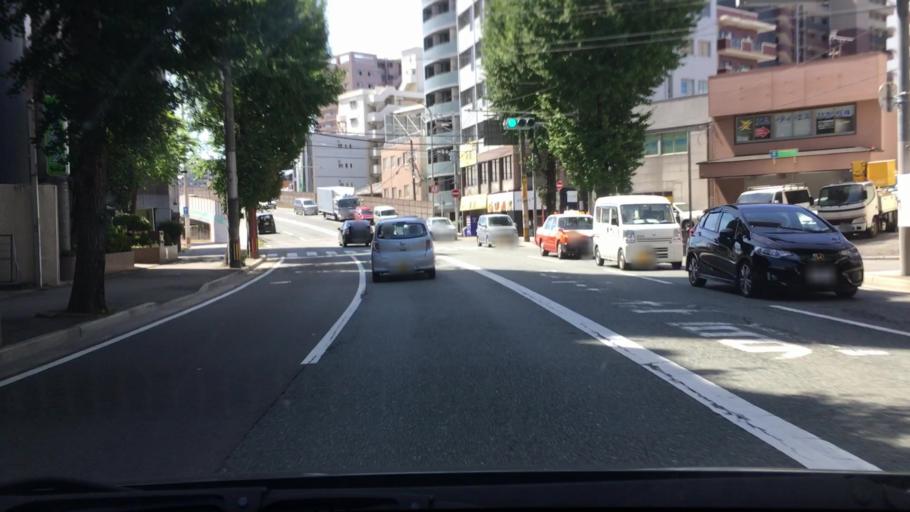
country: JP
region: Fukuoka
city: Fukuoka-shi
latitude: 33.5779
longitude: 130.4198
